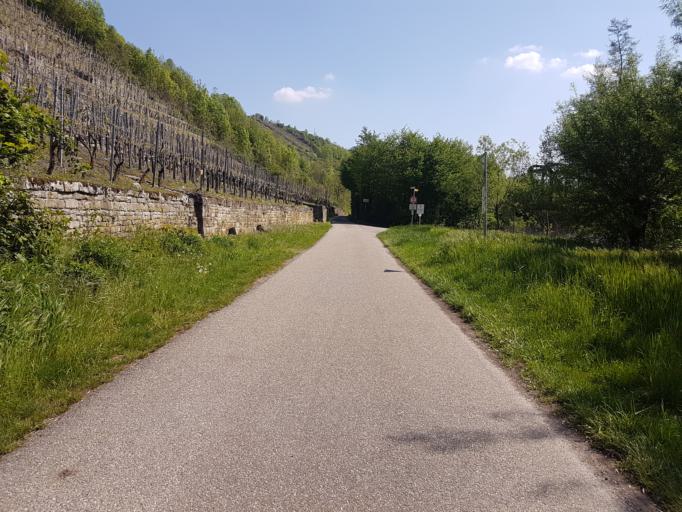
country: DE
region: Baden-Wuerttemberg
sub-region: Regierungsbezirk Stuttgart
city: Besigheim
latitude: 48.9900
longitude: 9.1504
